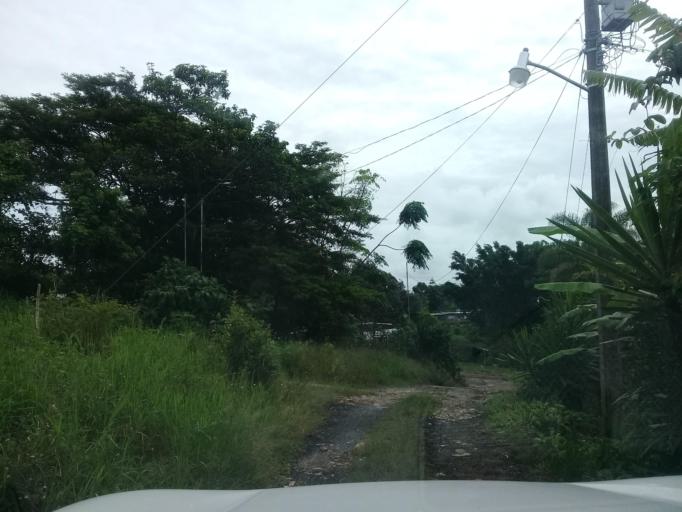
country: MX
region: Veracruz
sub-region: Emiliano Zapata
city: Jacarandas
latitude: 19.4831
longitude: -96.8580
